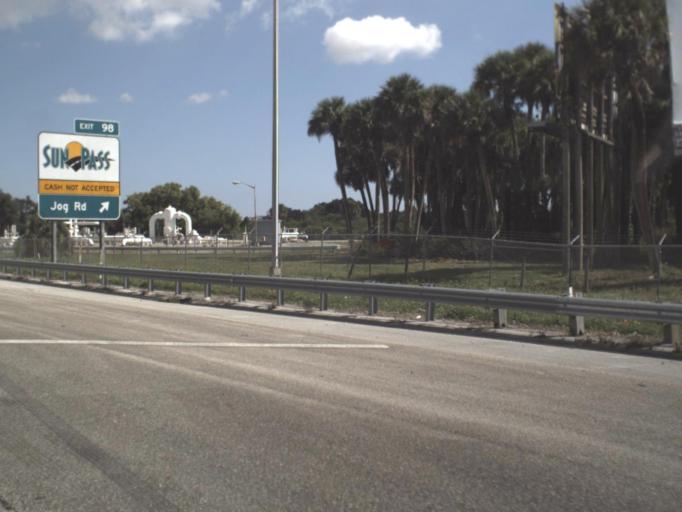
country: US
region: Florida
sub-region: Palm Beach County
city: Lake Belvedere Estates
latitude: 26.6952
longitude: -80.1531
